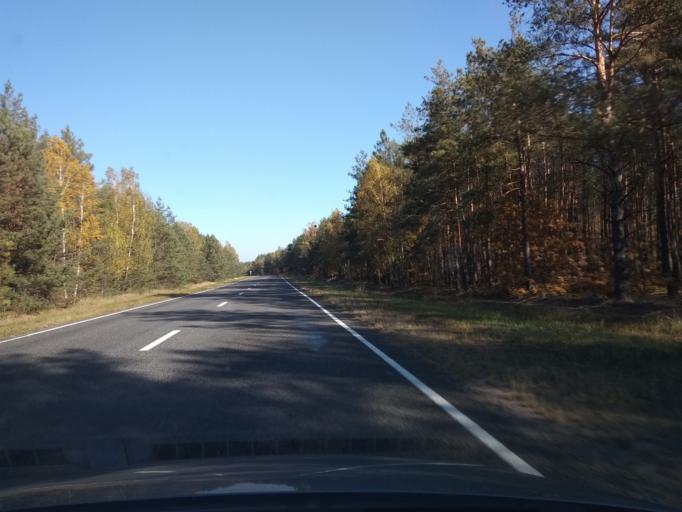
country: BY
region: Brest
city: Malaryta
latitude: 51.9618
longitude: 24.1921
